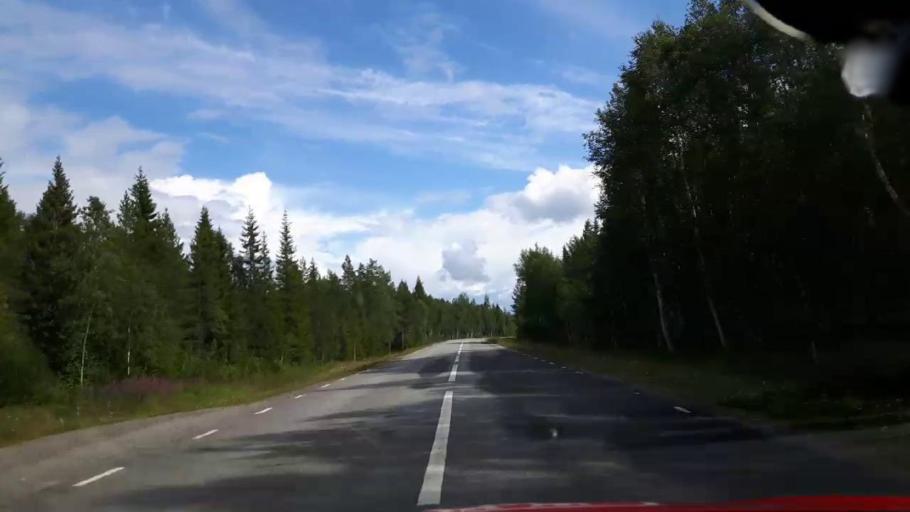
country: SE
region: Jaemtland
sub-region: Stroemsunds Kommun
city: Stroemsund
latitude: 64.3459
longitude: 15.0979
